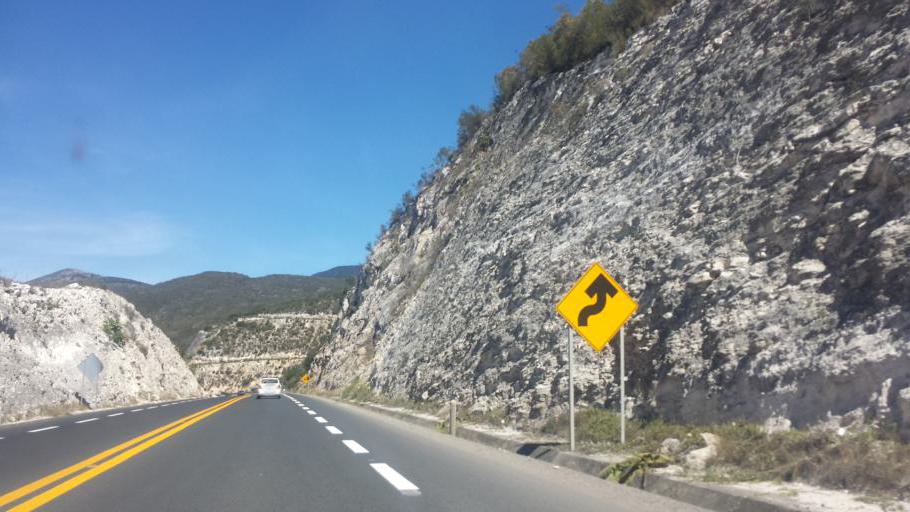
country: MX
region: Puebla
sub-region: San Jose Miahuatlan
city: San Pedro Tetitlan
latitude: 18.0150
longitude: -97.3540
